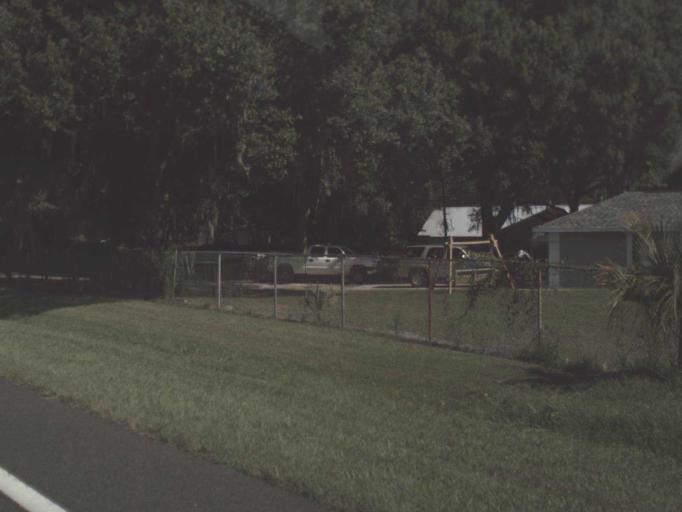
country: US
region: Florida
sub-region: Polk County
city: Willow Oak
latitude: 27.9338
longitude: -82.0839
